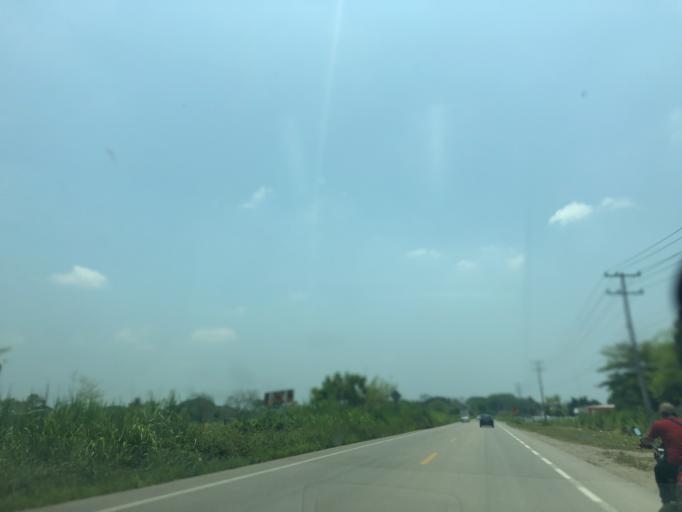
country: MX
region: Tabasco
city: Teapa
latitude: 17.5837
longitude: -92.9680
